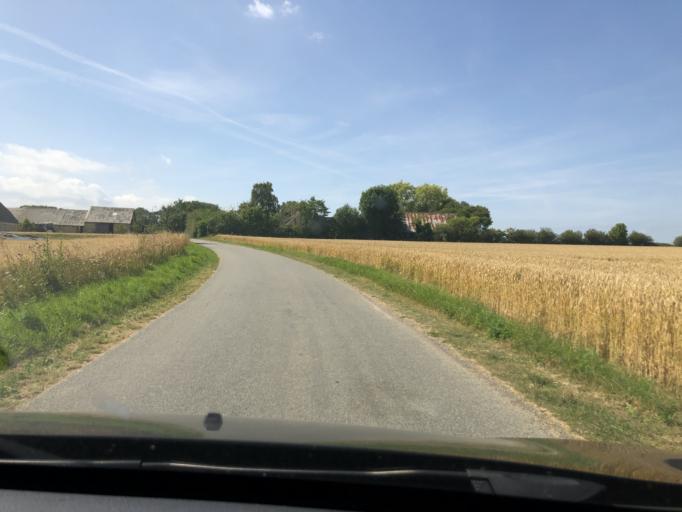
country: DK
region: South Denmark
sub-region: AEro Kommune
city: AEroskobing
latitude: 54.8918
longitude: 10.3031
